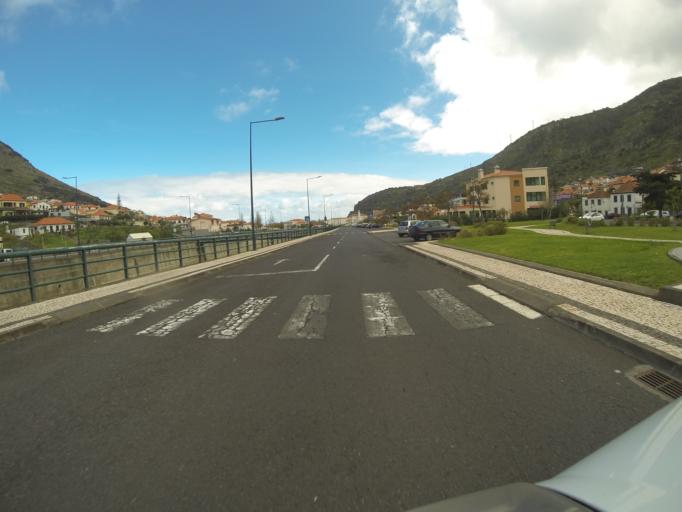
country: PT
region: Madeira
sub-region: Machico
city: Machico
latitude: 32.7193
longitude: -16.7671
